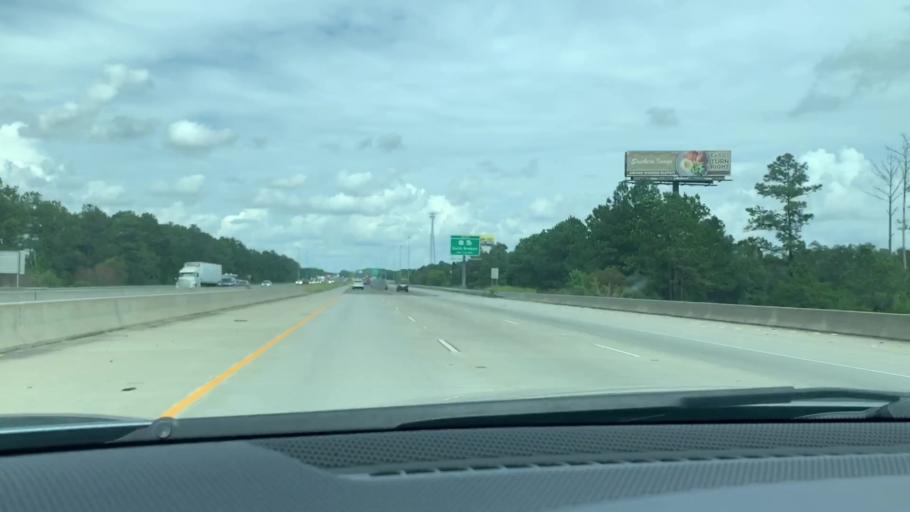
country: US
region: Georgia
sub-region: Liberty County
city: Midway
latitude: 31.6449
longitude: -81.3992
